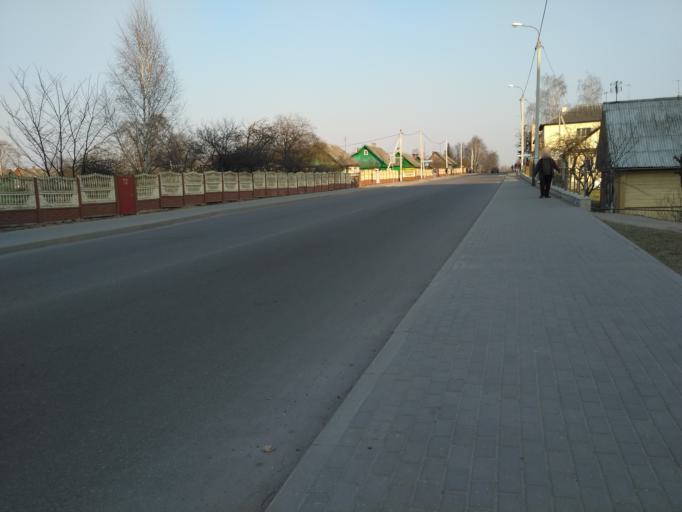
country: BY
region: Minsk
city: Zaslawye
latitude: 54.0082
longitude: 27.2778
